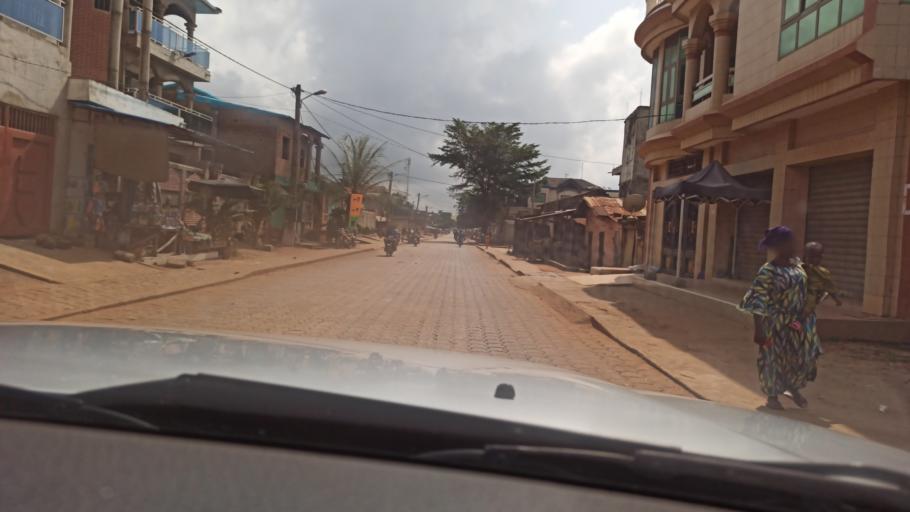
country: BJ
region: Queme
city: Porto-Novo
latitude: 6.4687
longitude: 2.6430
